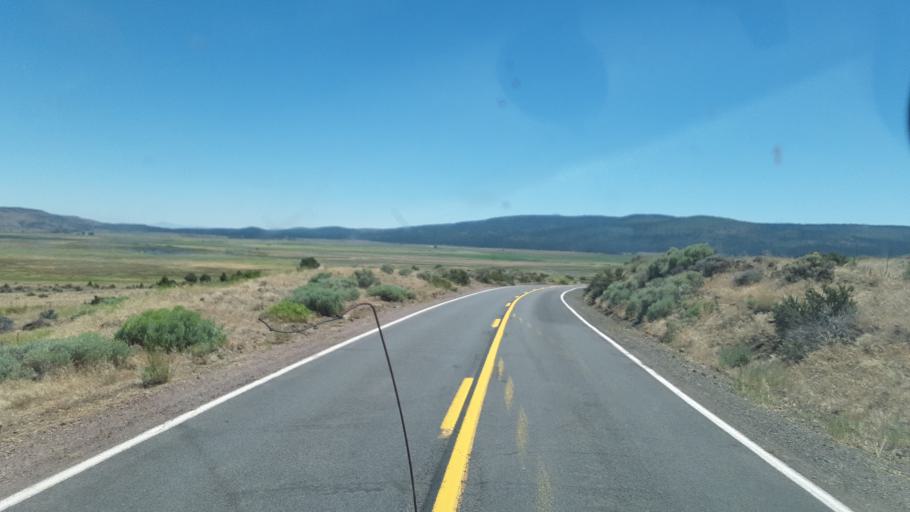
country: US
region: California
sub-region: Lassen County
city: Susanville
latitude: 40.5860
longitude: -120.6400
